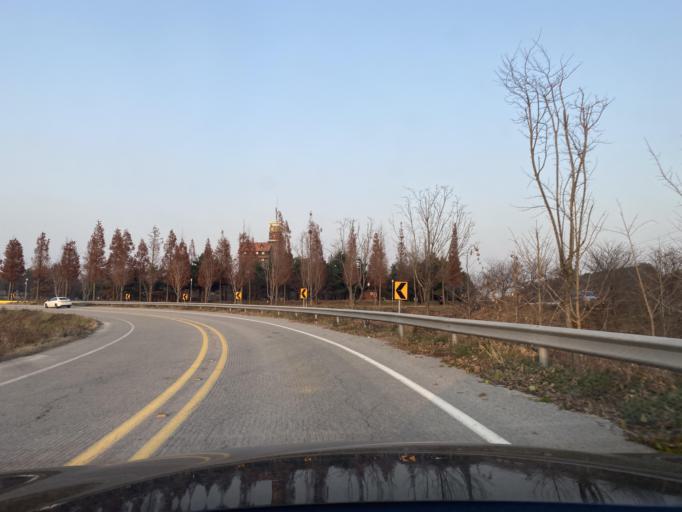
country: KR
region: Chungcheongnam-do
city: Hongsung
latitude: 36.6859
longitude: 126.6597
